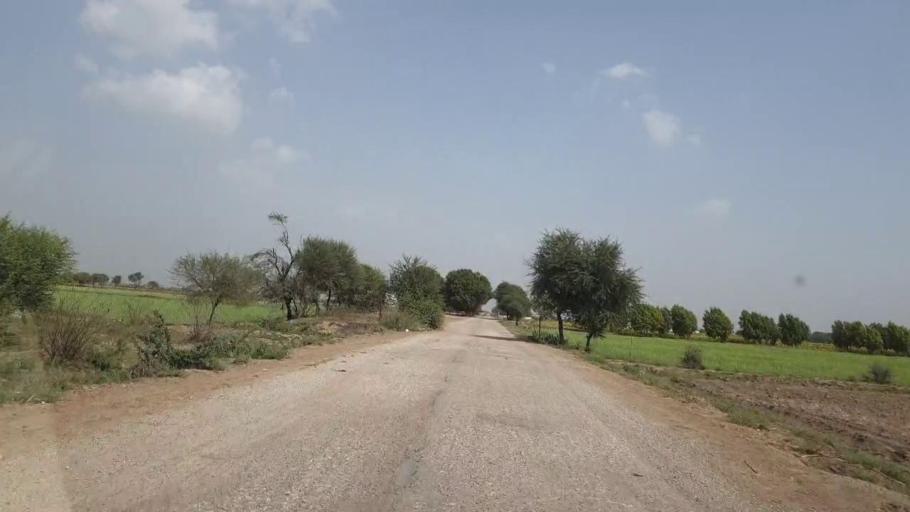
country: PK
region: Sindh
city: Rajo Khanani
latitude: 25.0499
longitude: 68.8713
